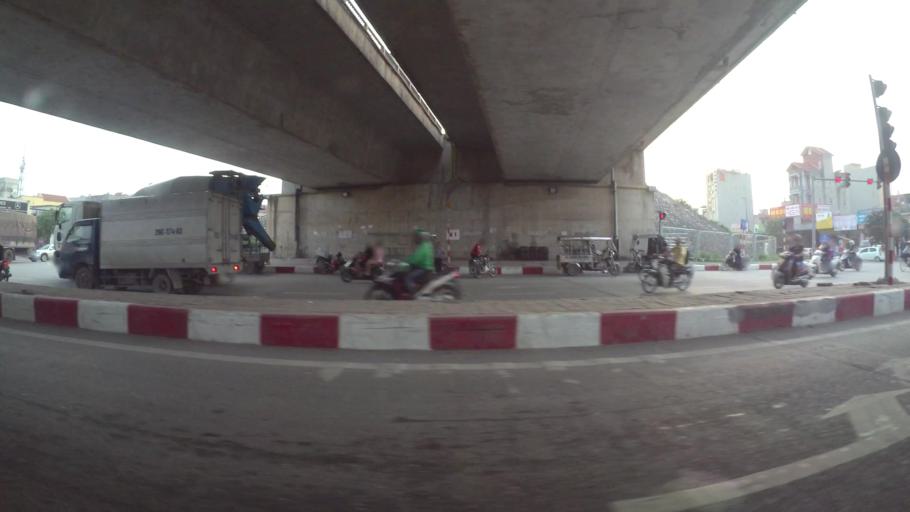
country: VN
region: Ha Noi
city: Van Dien
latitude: 20.9642
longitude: 105.8687
